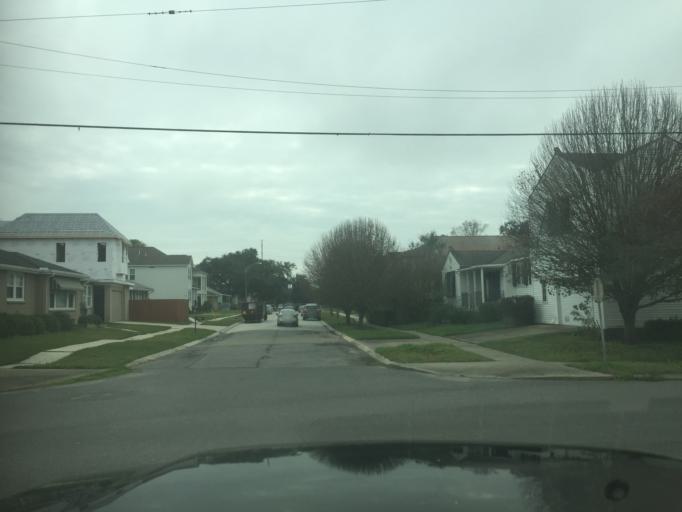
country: US
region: Louisiana
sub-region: Jefferson Parish
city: Metairie
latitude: 30.0026
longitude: -90.1050
